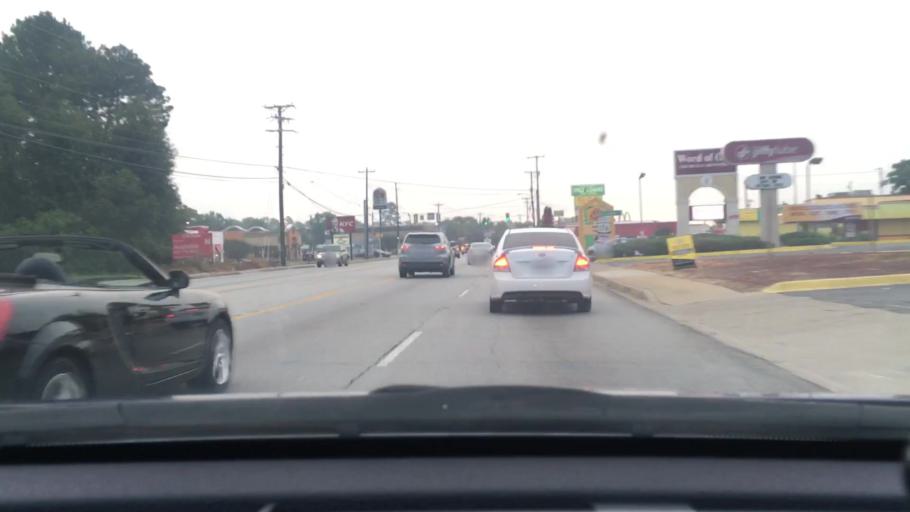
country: US
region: South Carolina
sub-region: Lexington County
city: Saint Andrews
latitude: 34.0381
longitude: -81.0921
